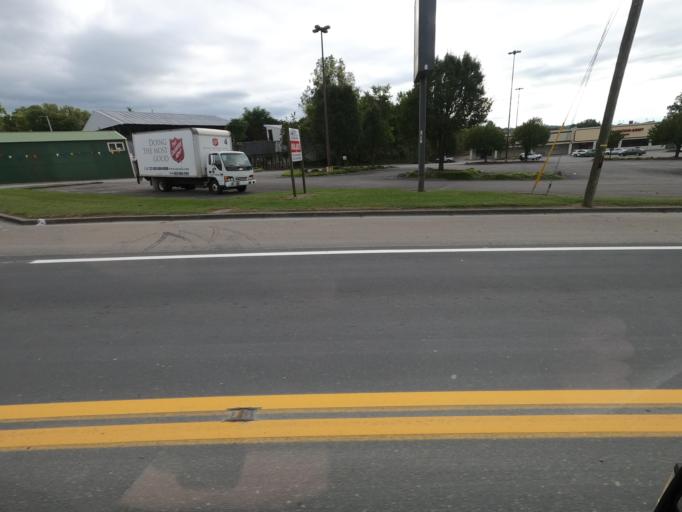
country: US
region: Tennessee
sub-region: Washington County
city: Johnson City
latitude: 36.3253
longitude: -82.3306
